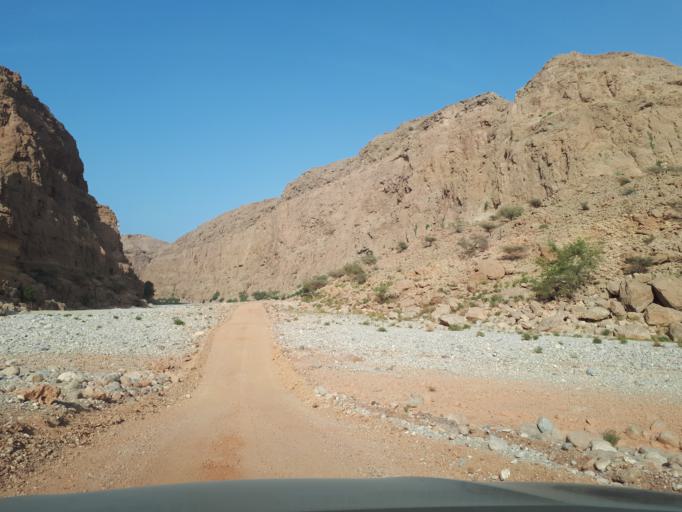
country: OM
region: Ash Sharqiyah
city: Al Qabil
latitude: 23.0741
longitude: 59.0162
